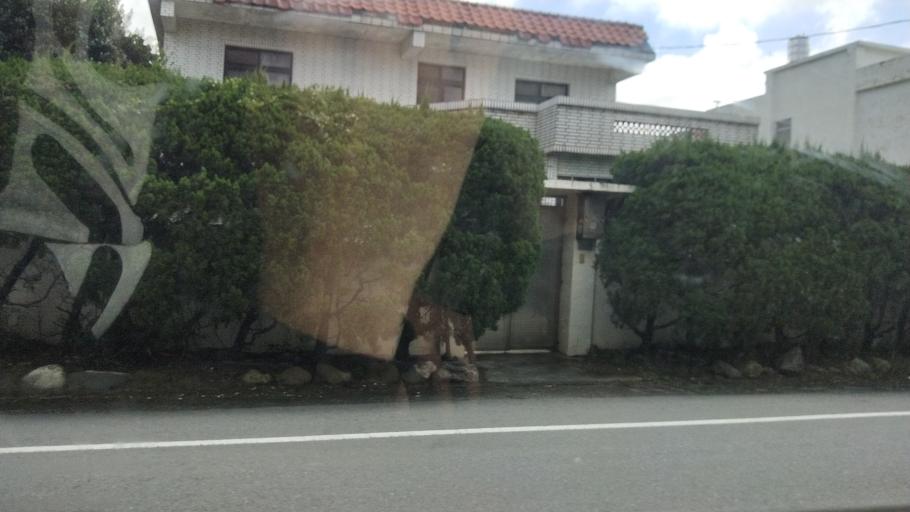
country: TW
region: Taiwan
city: Taoyuan City
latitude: 25.0180
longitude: 121.1377
